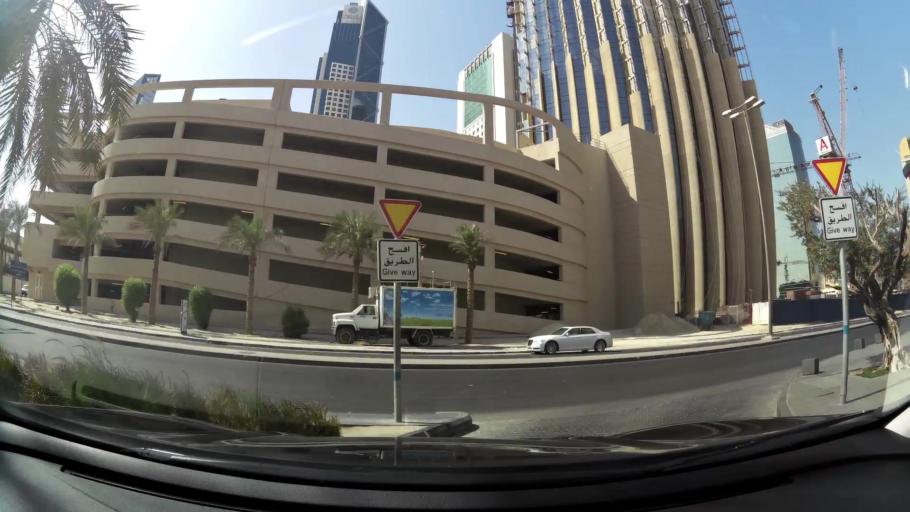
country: KW
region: Al Asimah
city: Ad Dasmah
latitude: 29.3777
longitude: 47.9929
